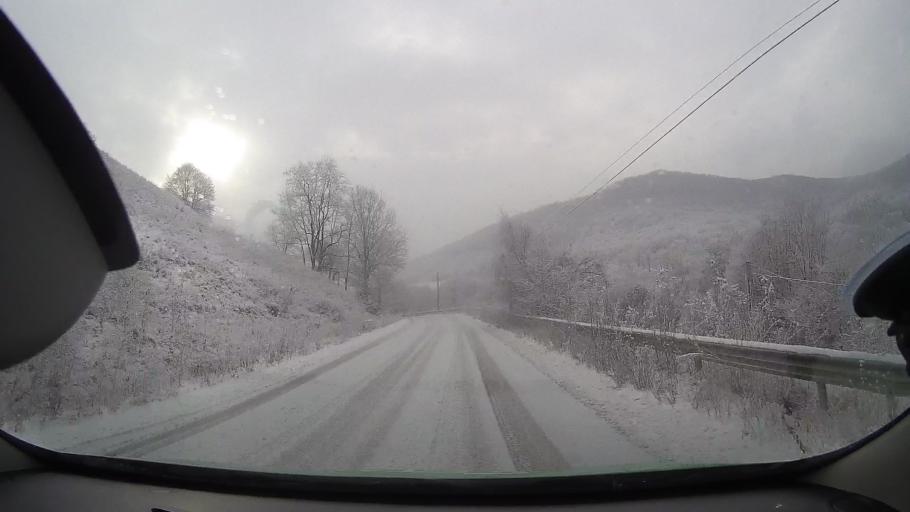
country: RO
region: Alba
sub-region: Comuna Rimetea
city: Rimetea
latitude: 46.4809
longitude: 23.5806
